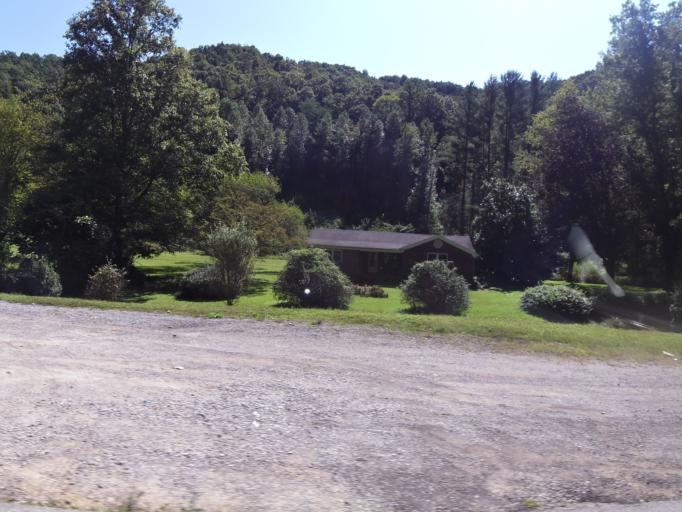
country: US
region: Kentucky
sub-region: Clay County
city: Manchester
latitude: 37.1387
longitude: -83.6125
